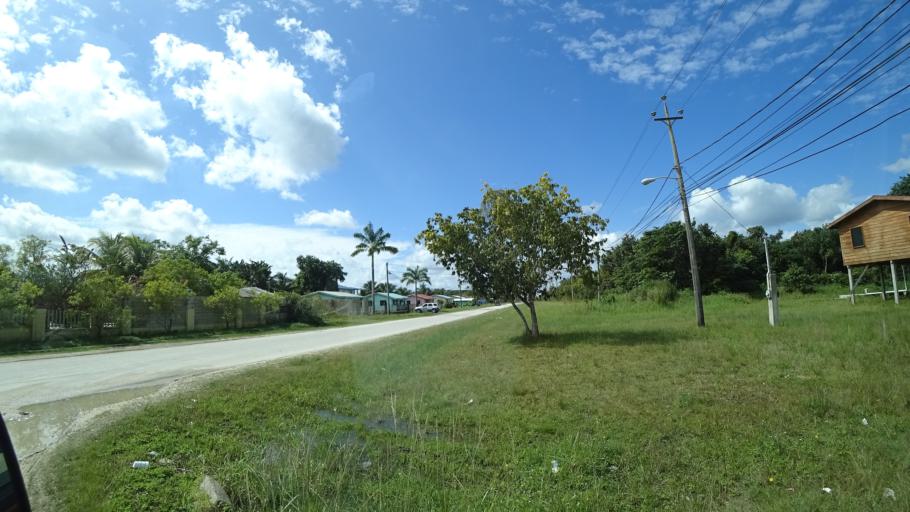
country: BZ
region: Belize
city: Belize City
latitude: 17.5690
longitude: -88.4142
